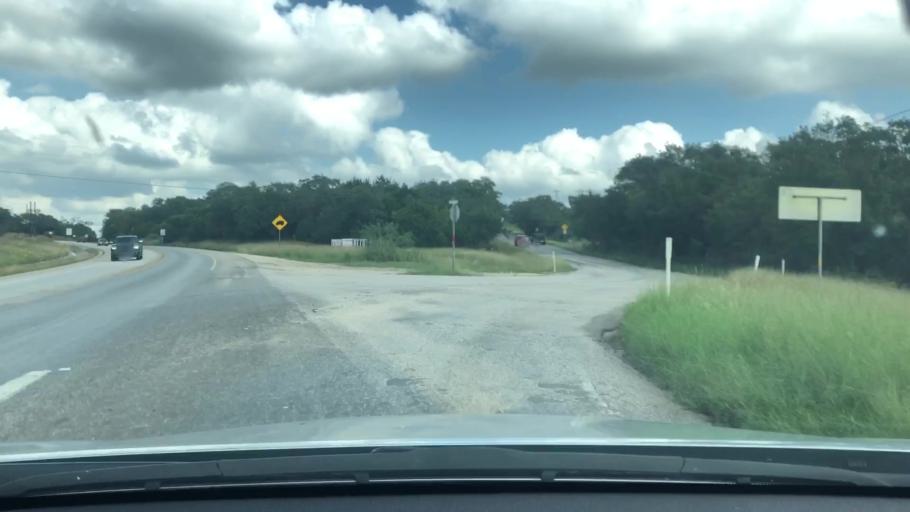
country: US
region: Texas
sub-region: Kendall County
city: Boerne
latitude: 29.7872
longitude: -98.6894
